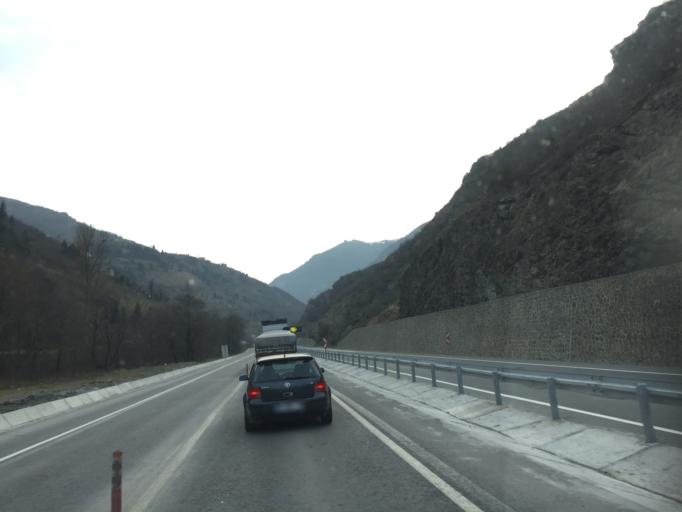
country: TR
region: Trabzon
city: Macka
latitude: 40.7945
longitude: 39.5830
